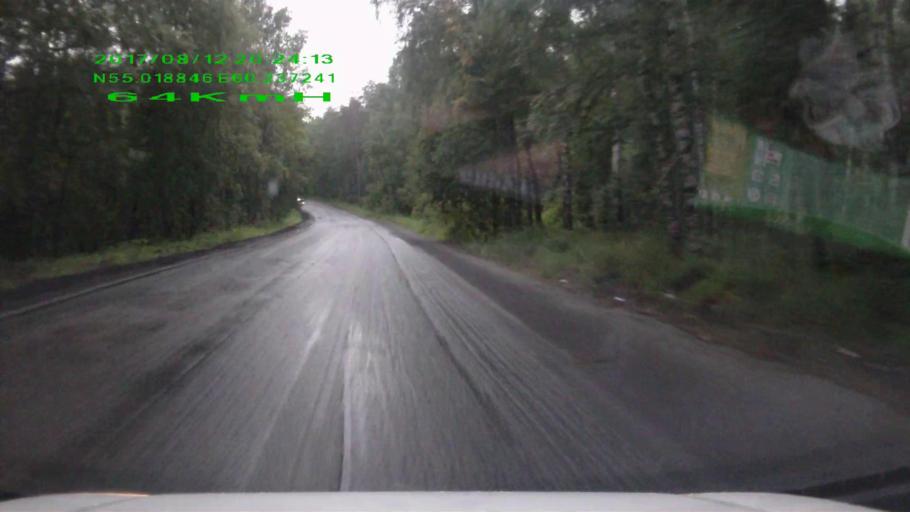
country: RU
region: Chelyabinsk
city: Miass
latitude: 55.0187
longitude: 60.2367
